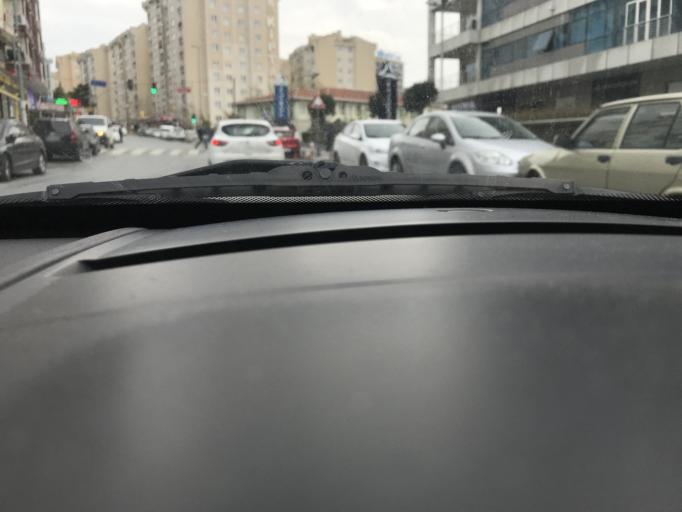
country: TR
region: Istanbul
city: Yakuplu
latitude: 41.0048
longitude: 28.6903
